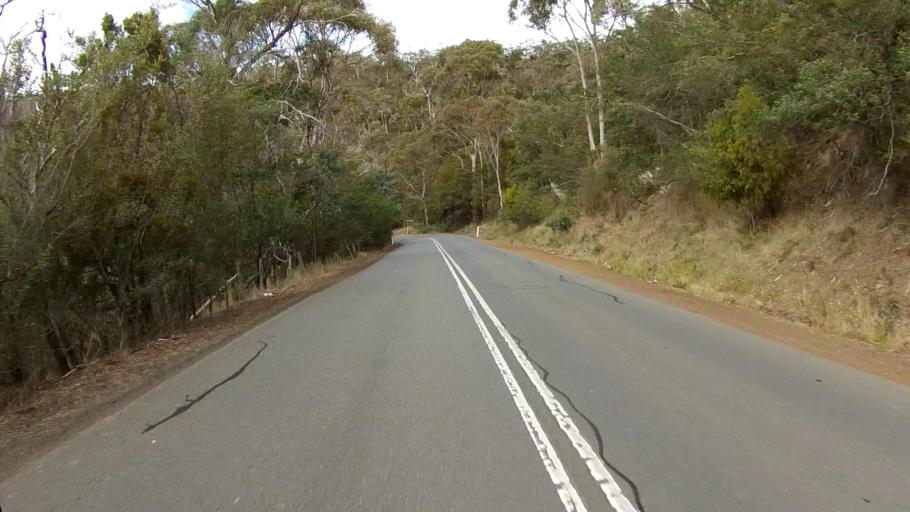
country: AU
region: Tasmania
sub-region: Clarence
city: Lindisfarne
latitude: -42.7803
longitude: 147.3700
